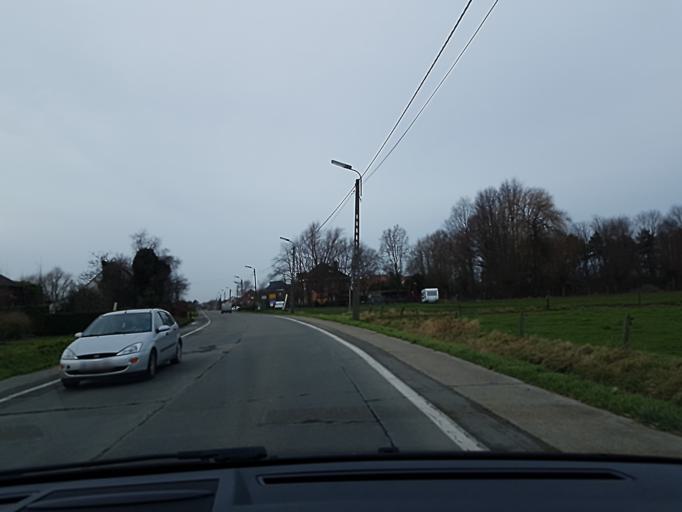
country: BE
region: Flanders
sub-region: Provincie Antwerpen
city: Putte
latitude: 51.0637
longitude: 4.6069
